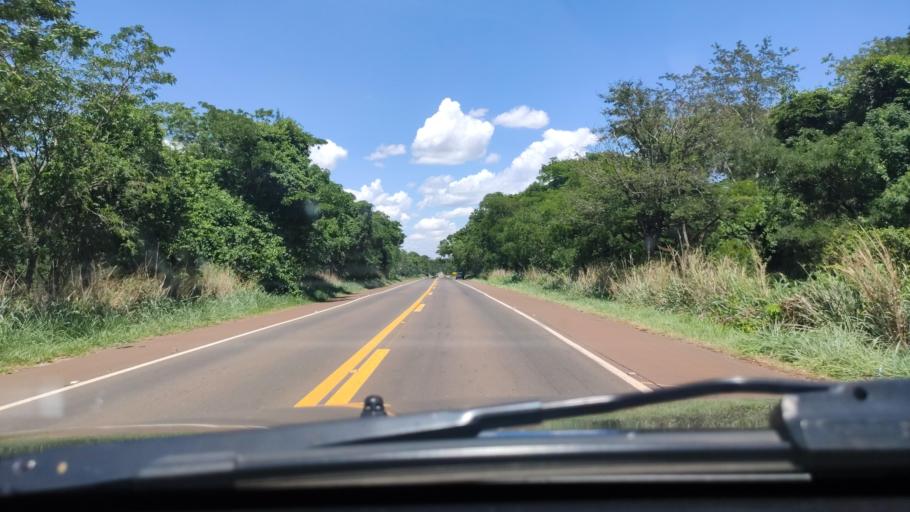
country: BR
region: Sao Paulo
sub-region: Boa Esperanca Do Sul
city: Boa Esperanca do Sul
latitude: -22.0690
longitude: -48.3699
